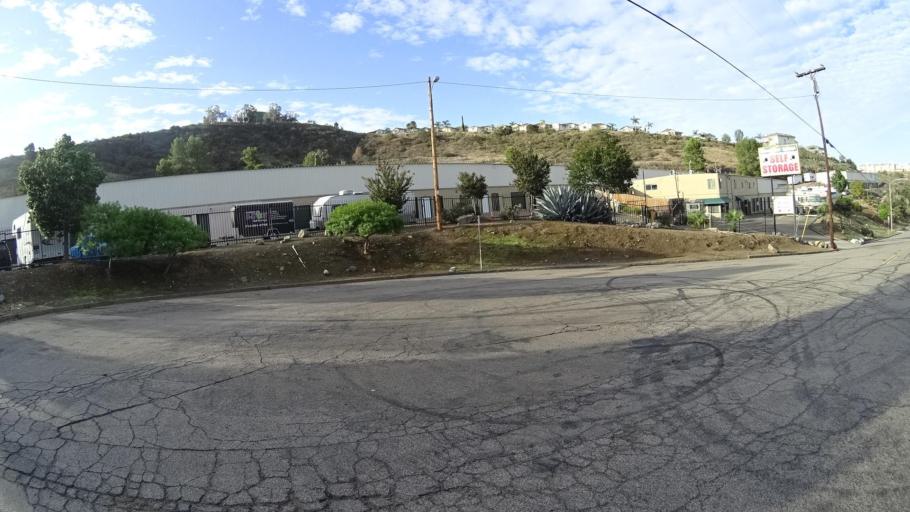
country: US
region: California
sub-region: San Diego County
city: La Presa
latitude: 32.7219
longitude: -116.9632
